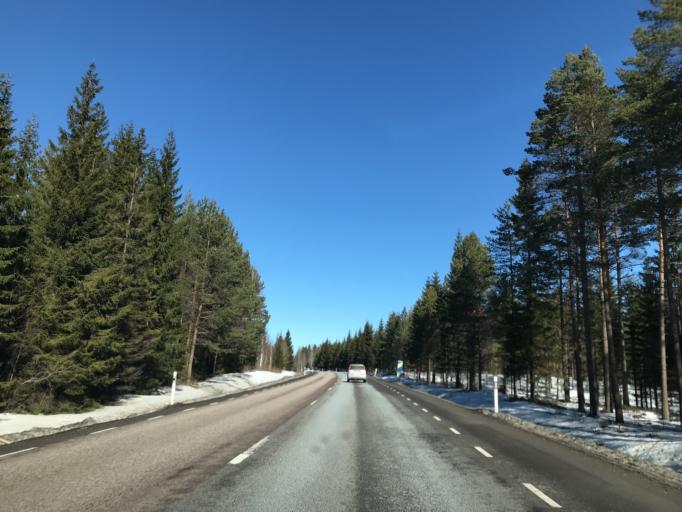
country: SE
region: Vaermland
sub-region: Filipstads Kommun
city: Filipstad
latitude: 59.7430
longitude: 14.2347
